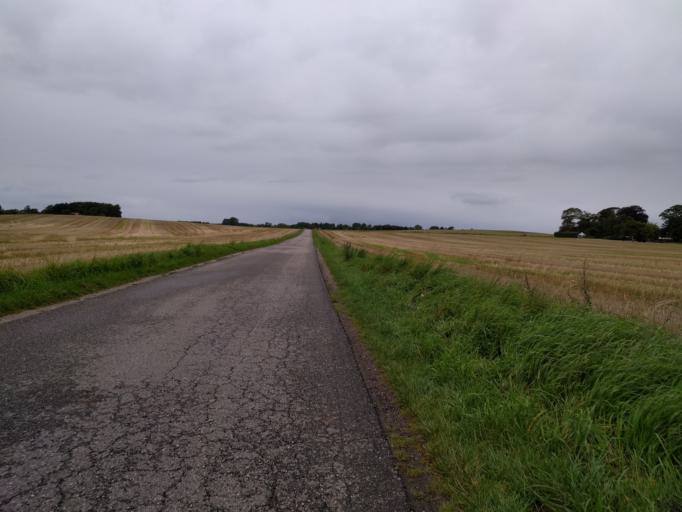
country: DK
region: South Denmark
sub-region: Kerteminde Kommune
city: Kerteminde
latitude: 55.4345
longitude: 10.6152
